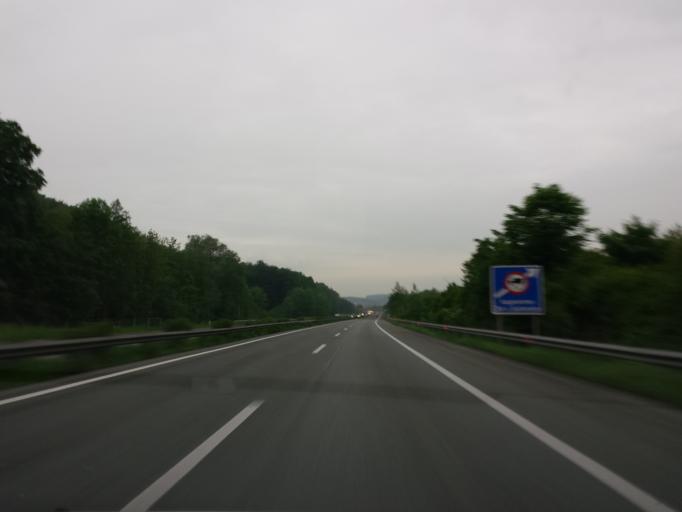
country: AT
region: Styria
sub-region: Politischer Bezirk Weiz
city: Sinabelkirchen
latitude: 47.0924
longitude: 15.8342
